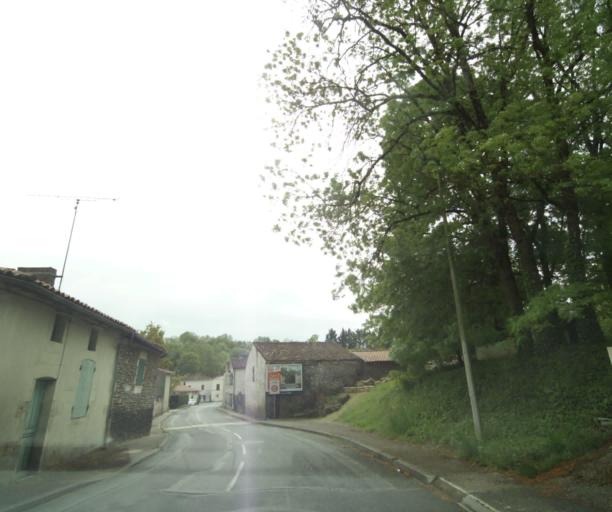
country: FR
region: Poitou-Charentes
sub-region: Departement de la Charente-Maritime
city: Chaniers
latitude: 45.7592
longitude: -0.5422
